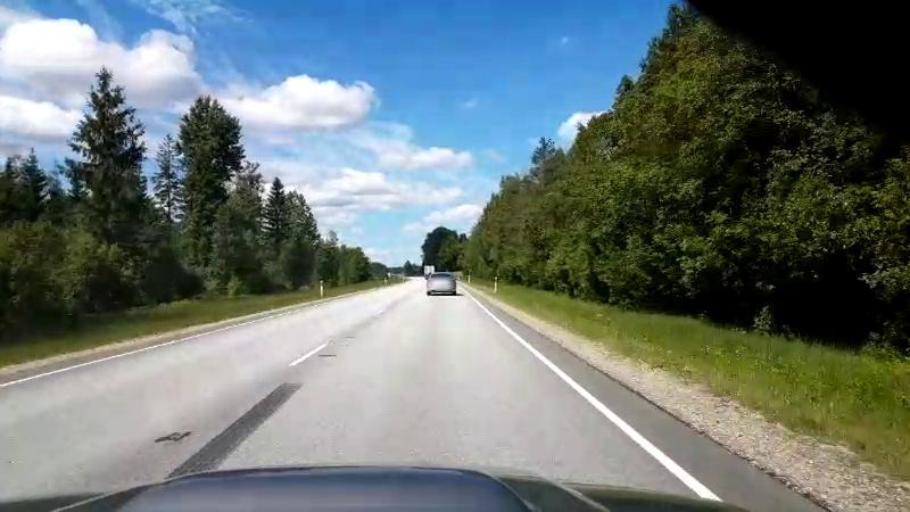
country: EE
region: Paernumaa
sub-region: Halinga vald
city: Parnu-Jaagupi
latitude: 58.5567
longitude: 24.5265
